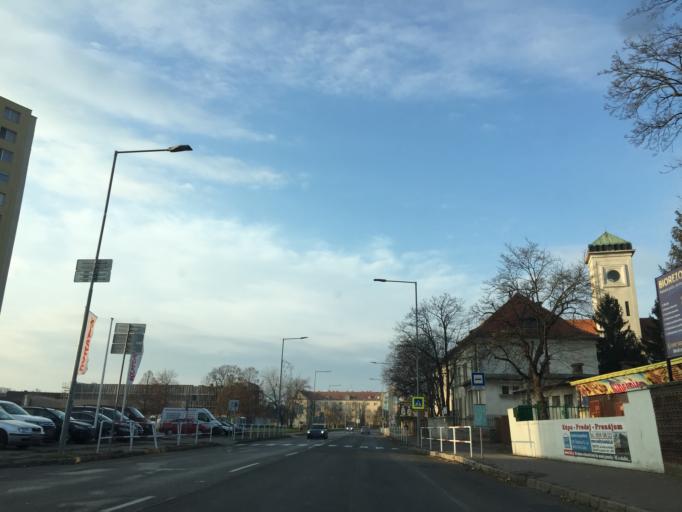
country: SK
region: Nitriansky
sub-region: Okres Nove Zamky
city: Nove Zamky
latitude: 47.9863
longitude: 18.1739
